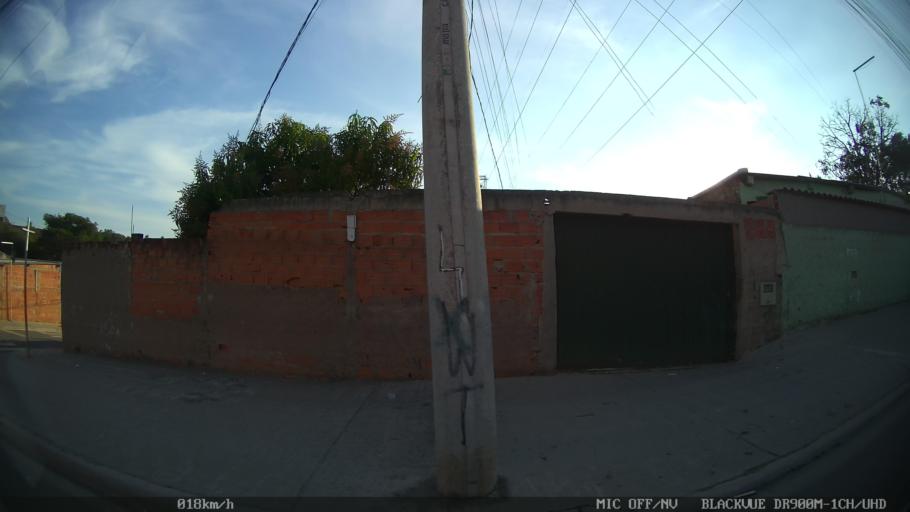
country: BR
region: Sao Paulo
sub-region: Campinas
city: Campinas
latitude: -22.9945
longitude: -47.1201
